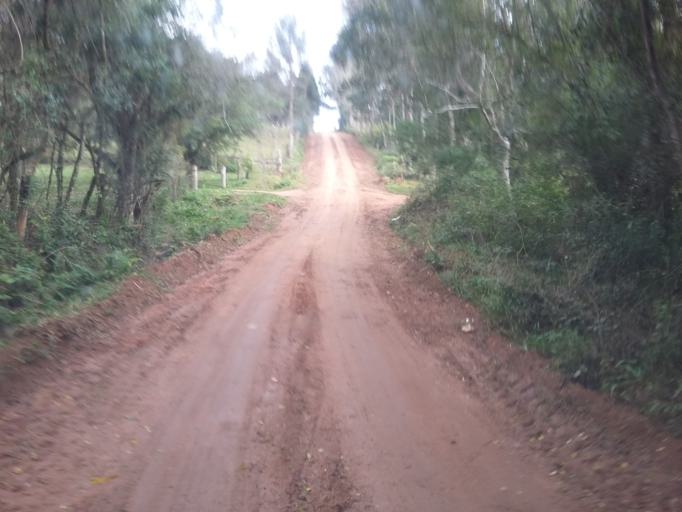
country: BR
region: Rio Grande do Sul
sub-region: Camaqua
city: Camaqua
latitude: -30.7109
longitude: -51.7763
